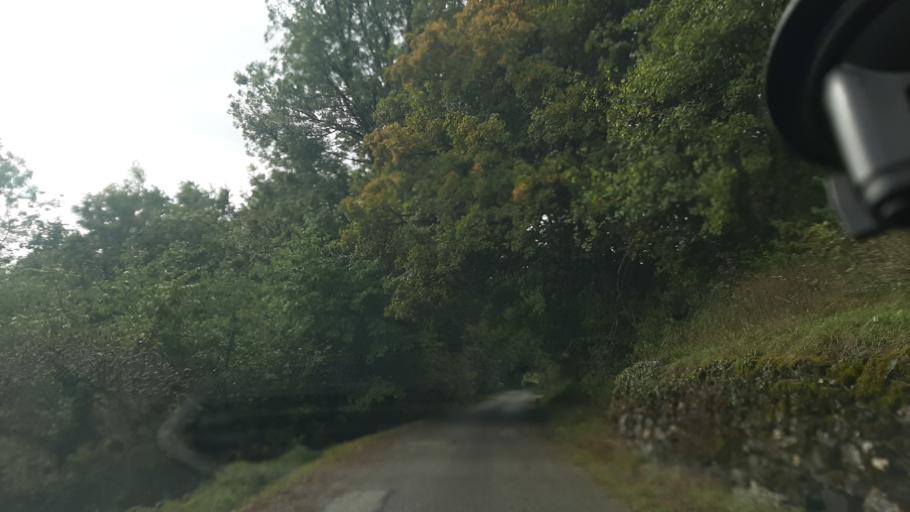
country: FR
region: Rhone-Alpes
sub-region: Departement de la Savoie
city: Gresy-sur-Isere
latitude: 45.6147
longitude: 6.2699
